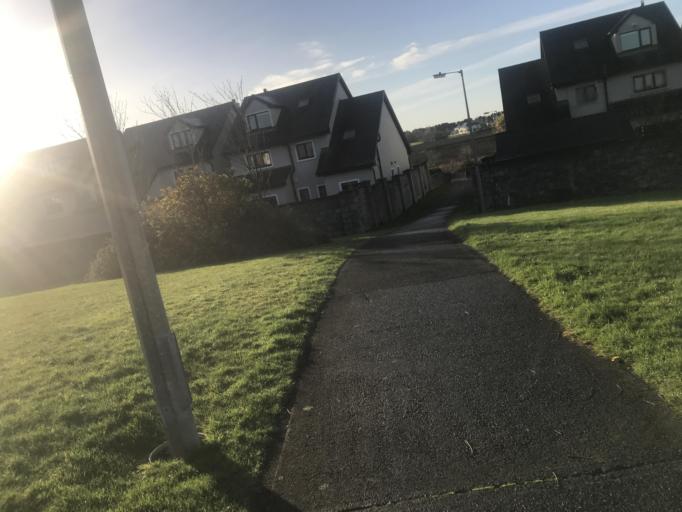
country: IE
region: Connaught
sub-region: County Galway
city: Oranmore
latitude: 53.2617
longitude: -8.9356
